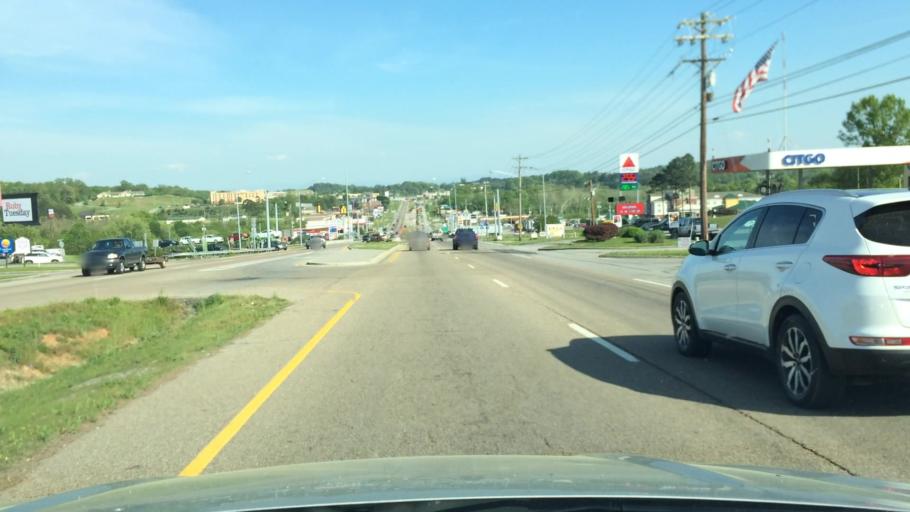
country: US
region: Tennessee
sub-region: Loudon County
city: Lenoir City
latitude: 35.8299
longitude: -84.2817
